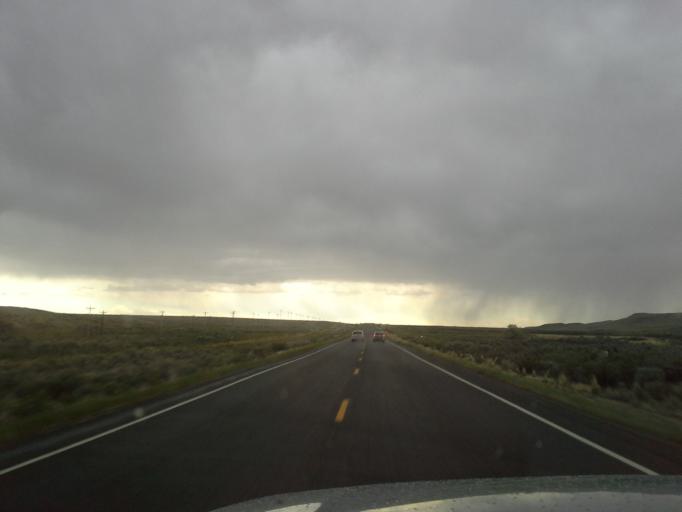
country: US
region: Wyoming
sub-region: Park County
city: Powell
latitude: 45.0452
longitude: -108.6511
